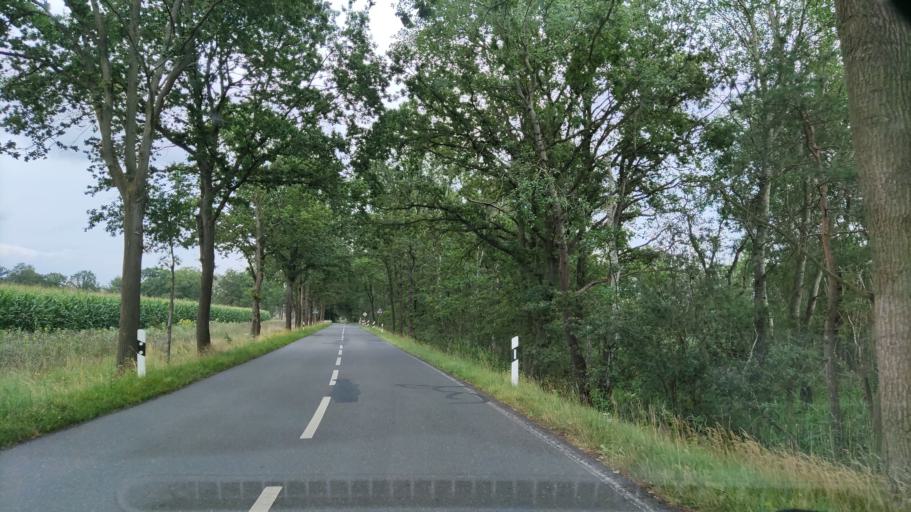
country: DE
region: Lower Saxony
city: Klein Gusborn
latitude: 53.0483
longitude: 11.1657
